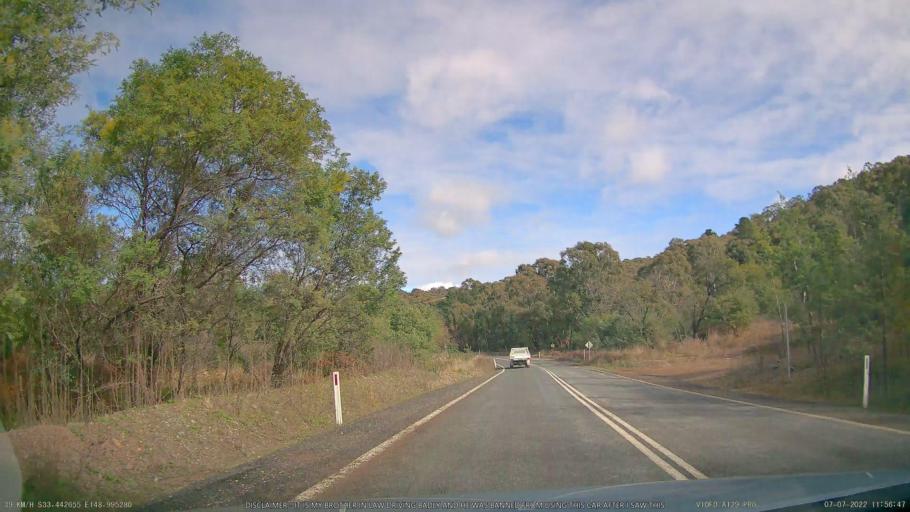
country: AU
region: New South Wales
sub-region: Blayney
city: Millthorpe
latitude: -33.4427
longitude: 148.9950
